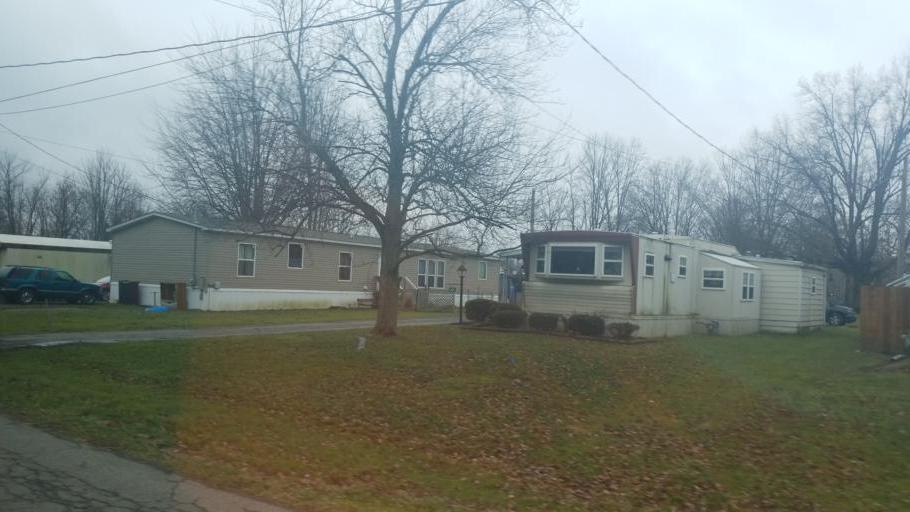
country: US
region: Ohio
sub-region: Crawford County
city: Galion
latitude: 40.7293
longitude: -82.7711
